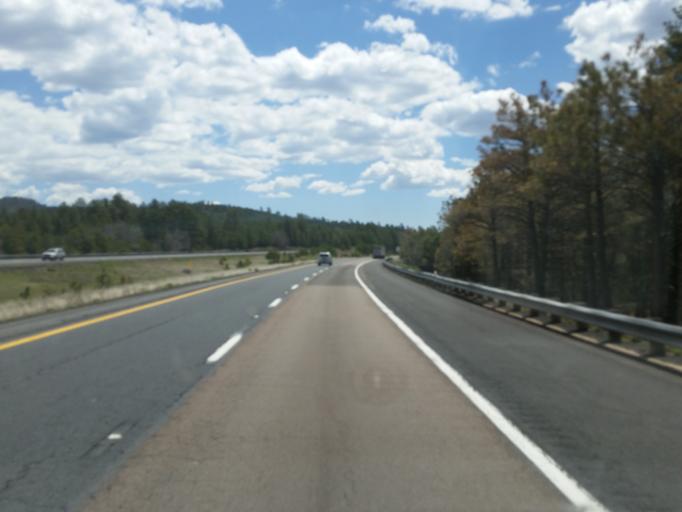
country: US
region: Arizona
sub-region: Coconino County
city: Parks
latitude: 35.2569
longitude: -111.9283
